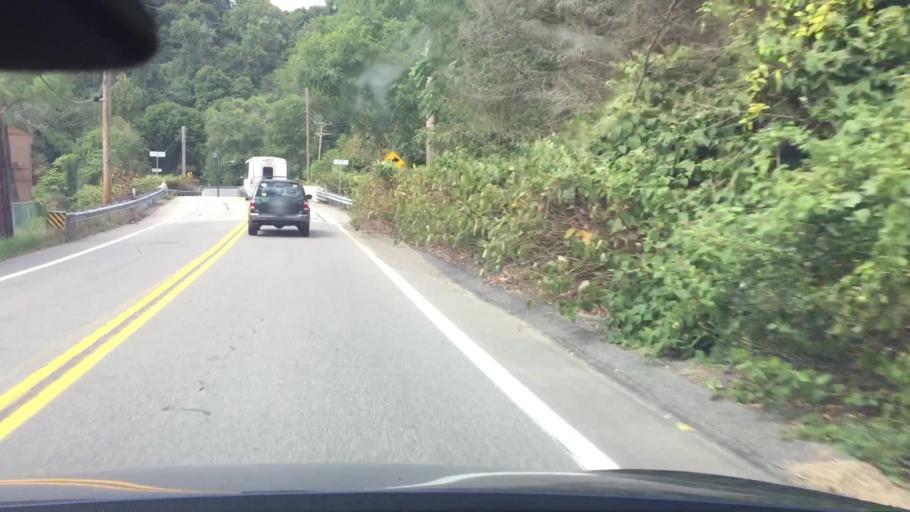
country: US
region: Pennsylvania
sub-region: Allegheny County
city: Cheswick
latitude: 40.5139
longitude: -79.8043
